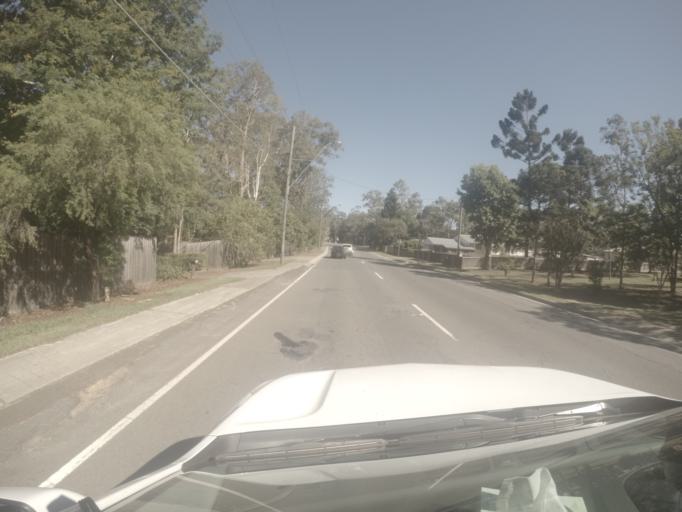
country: AU
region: Queensland
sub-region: Ipswich
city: Springfield
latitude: -27.6313
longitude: 152.9159
